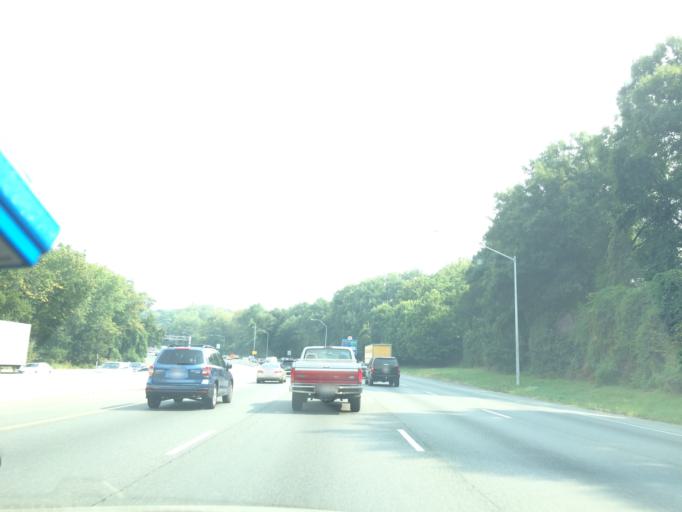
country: US
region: Maryland
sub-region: Montgomery County
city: South Kensington
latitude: 39.0093
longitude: -77.0885
